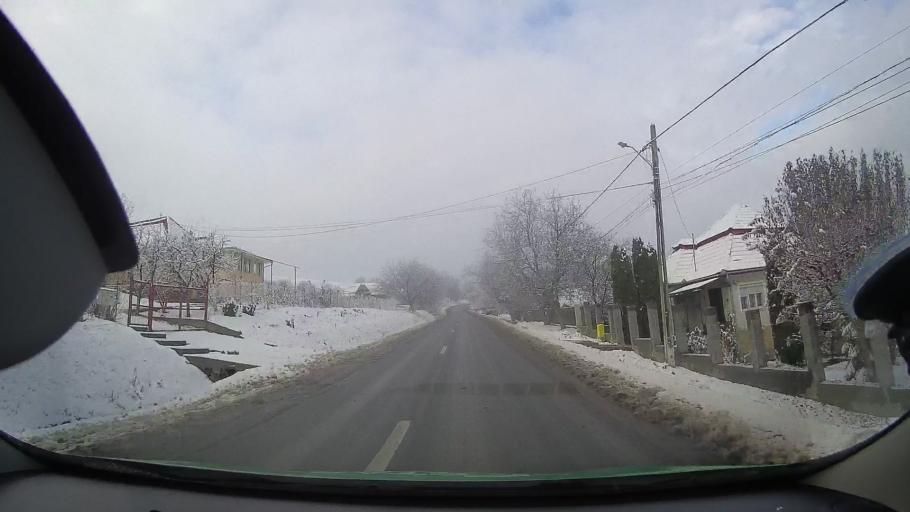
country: RO
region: Mures
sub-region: Comuna Atintis
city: Atintis
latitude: 46.4340
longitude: 24.0981
